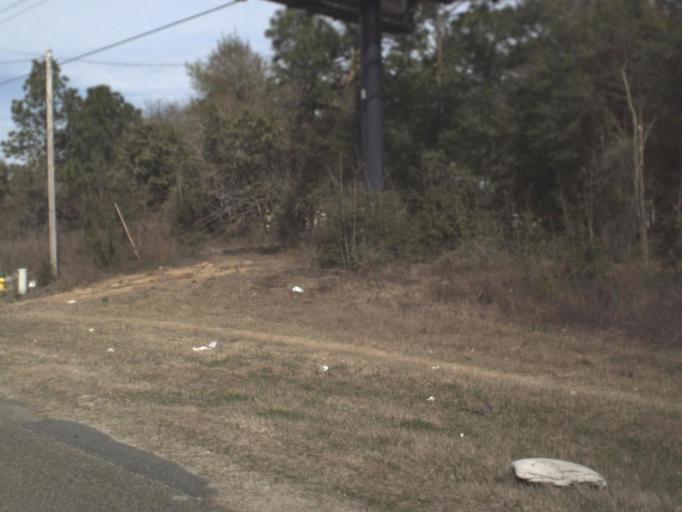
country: US
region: Florida
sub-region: Leon County
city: Tallahassee
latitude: 30.3824
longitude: -84.3063
